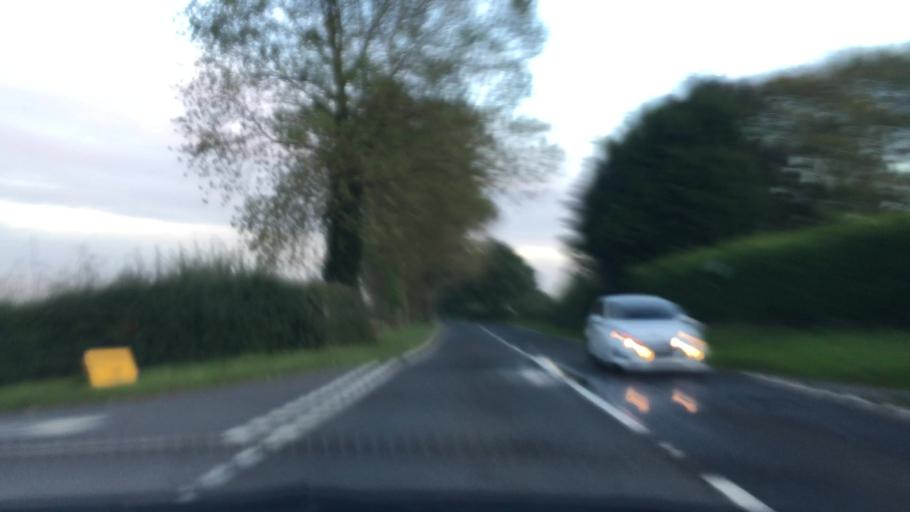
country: GB
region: England
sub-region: North East Lincolnshire
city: Wold Newton
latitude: 53.4656
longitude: -0.1029
